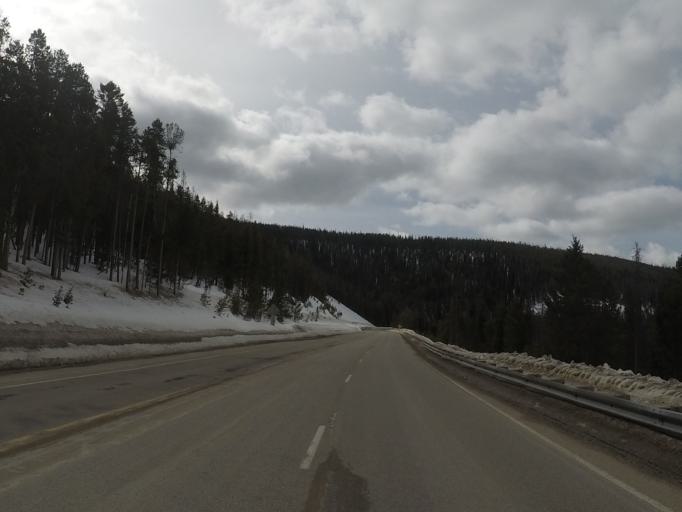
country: US
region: Idaho
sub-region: Lemhi County
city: Salmon
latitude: 45.7094
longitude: -113.9346
